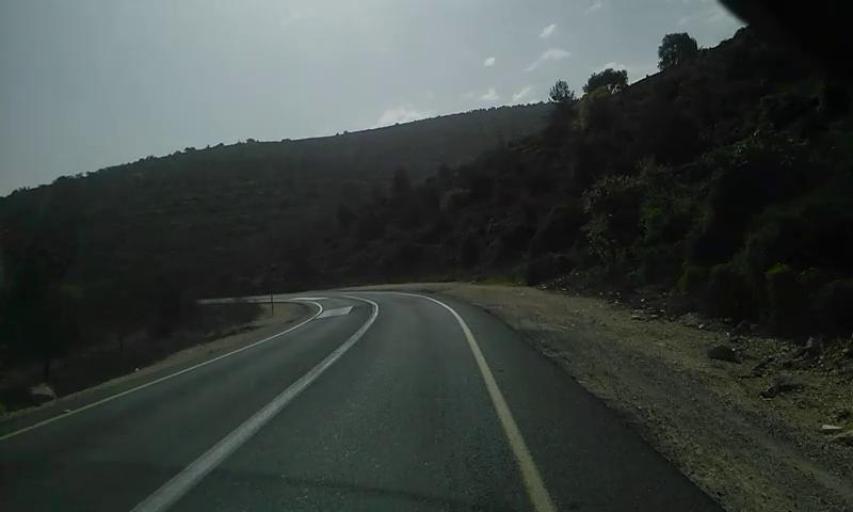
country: PS
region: West Bank
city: `Atarah
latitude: 31.9993
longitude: 35.2336
